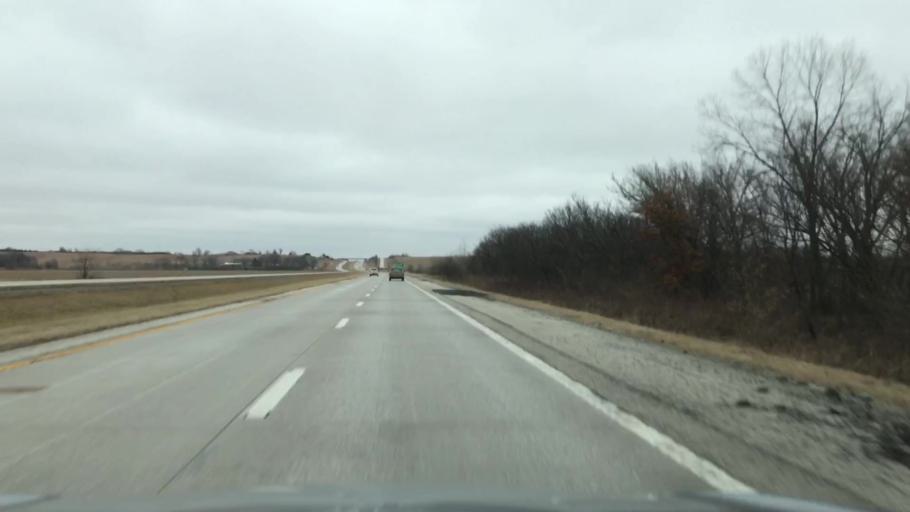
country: US
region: Missouri
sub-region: Linn County
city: Marceline
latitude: 39.7610
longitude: -92.9724
